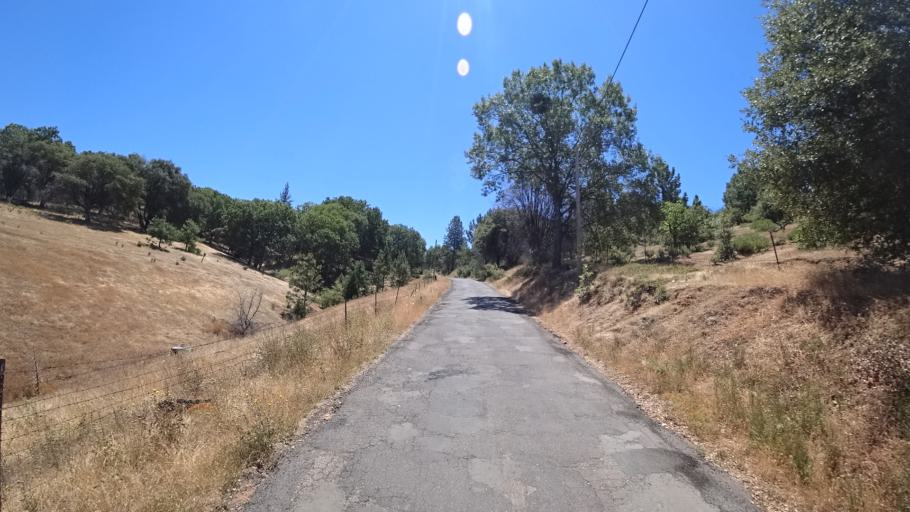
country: US
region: California
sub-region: Calaveras County
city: Mountain Ranch
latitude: 38.2323
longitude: -120.6028
